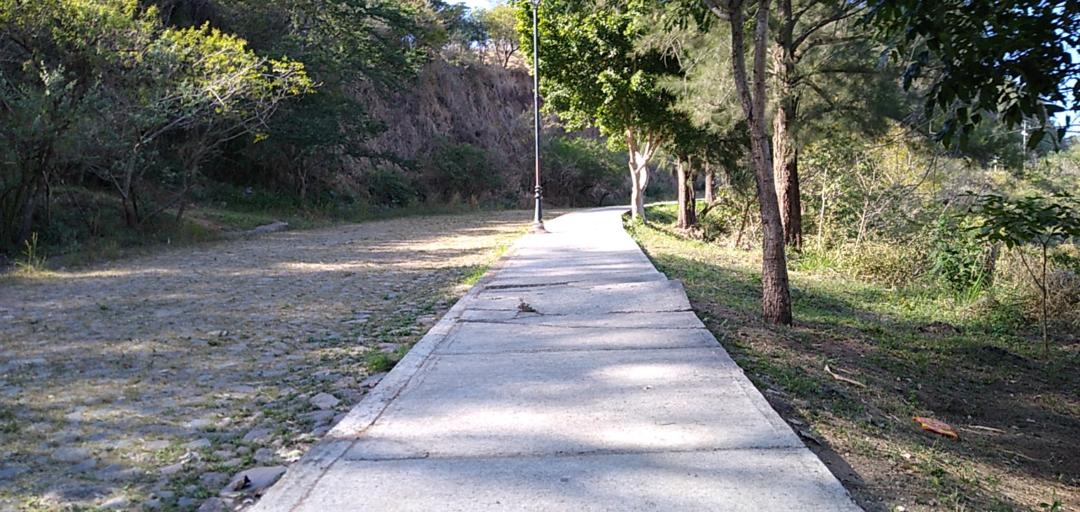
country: MX
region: Nayarit
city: Tepic
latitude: 21.5315
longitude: -104.8822
